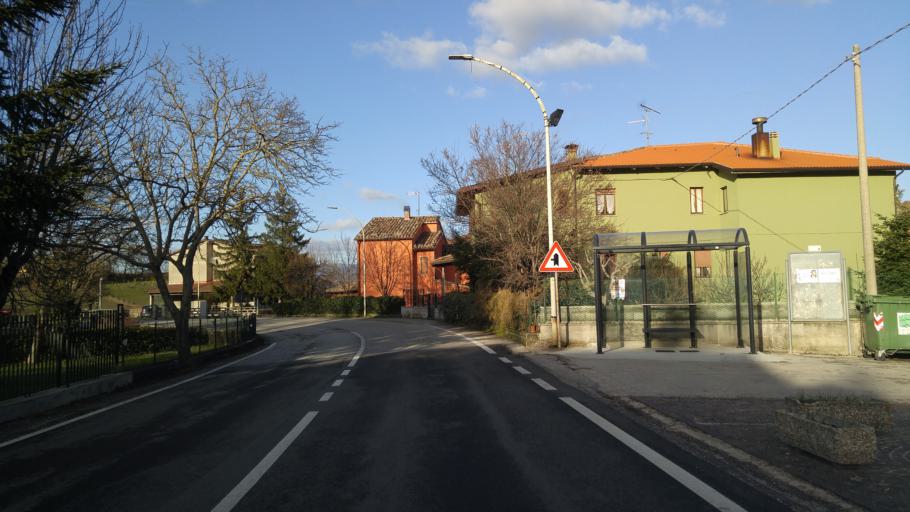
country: IT
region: The Marches
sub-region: Provincia di Pesaro e Urbino
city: Cagli
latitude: 43.5307
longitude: 12.6884
